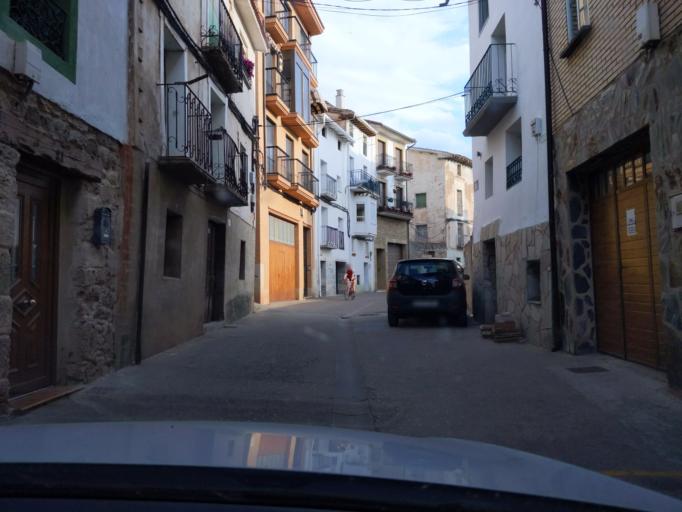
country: ES
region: La Rioja
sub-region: Provincia de La Rioja
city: Nalda
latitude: 42.3332
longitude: -2.4864
